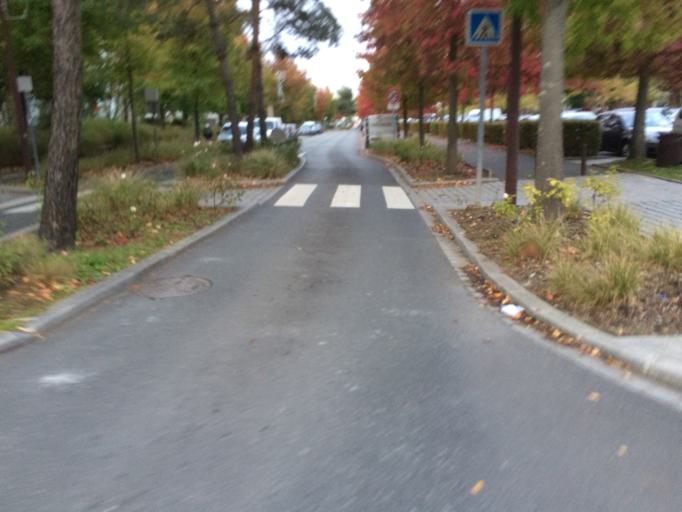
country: FR
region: Ile-de-France
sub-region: Departement de l'Essonne
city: Les Ulis
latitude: 48.6799
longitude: 2.1631
